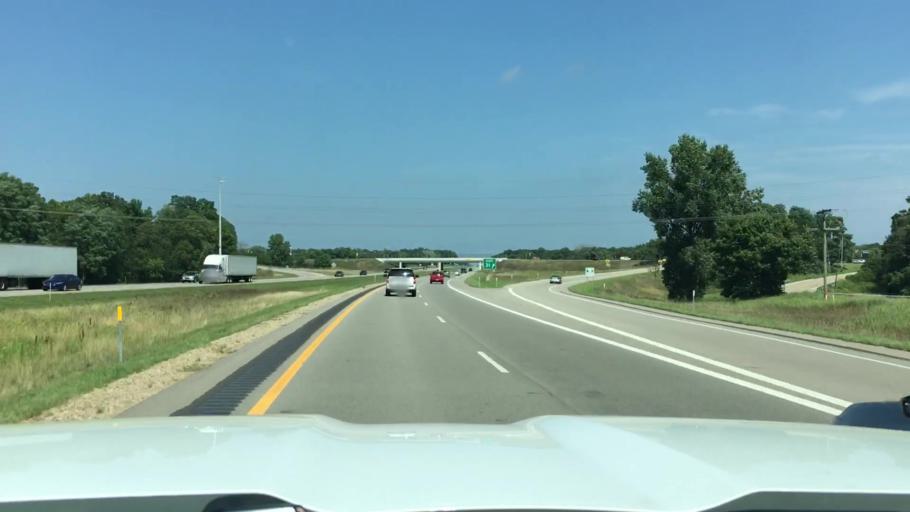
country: US
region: Michigan
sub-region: Kalamazoo County
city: Portage
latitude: 42.1952
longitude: -85.6463
